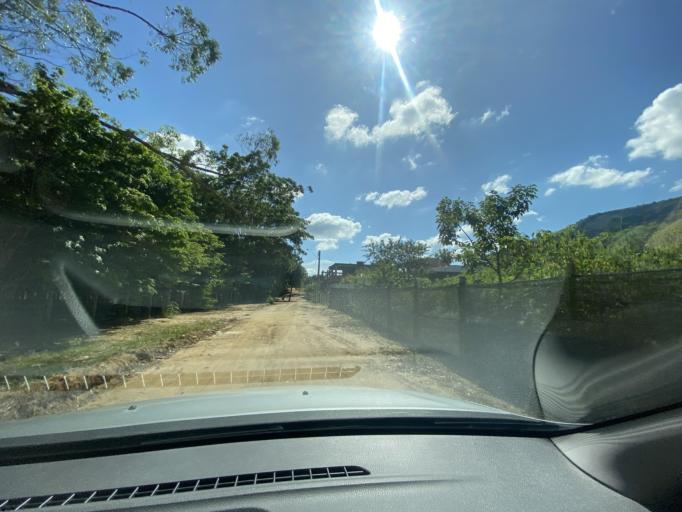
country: BR
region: Espirito Santo
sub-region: Jeronimo Monteiro
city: Jeronimo Monteiro
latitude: -20.7972
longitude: -41.4068
